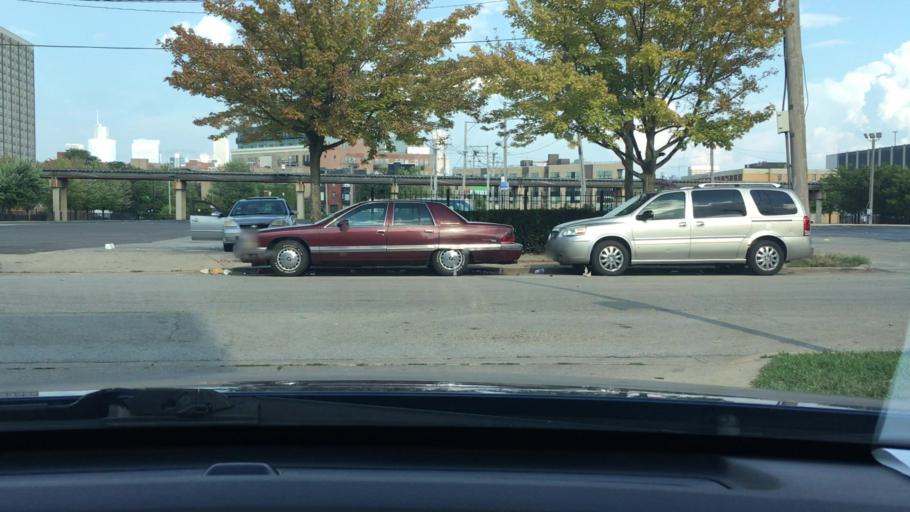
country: US
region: Illinois
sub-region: Cook County
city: Chicago
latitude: 41.8796
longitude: -87.6718
